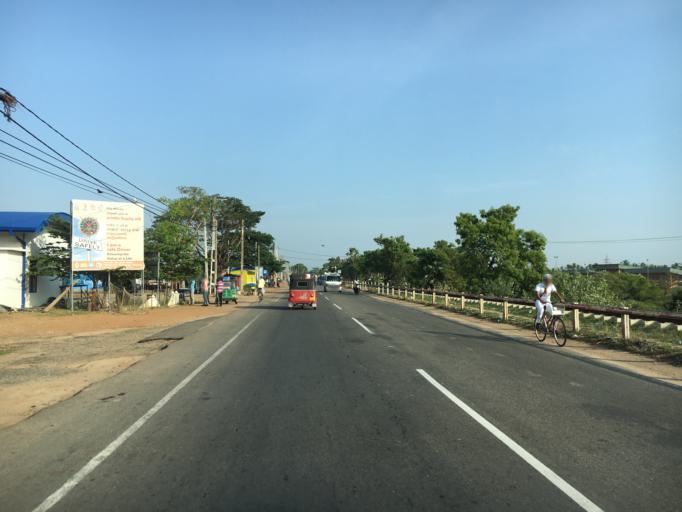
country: LK
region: Eastern Province
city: Eravur Town
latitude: 7.9171
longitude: 81.5197
